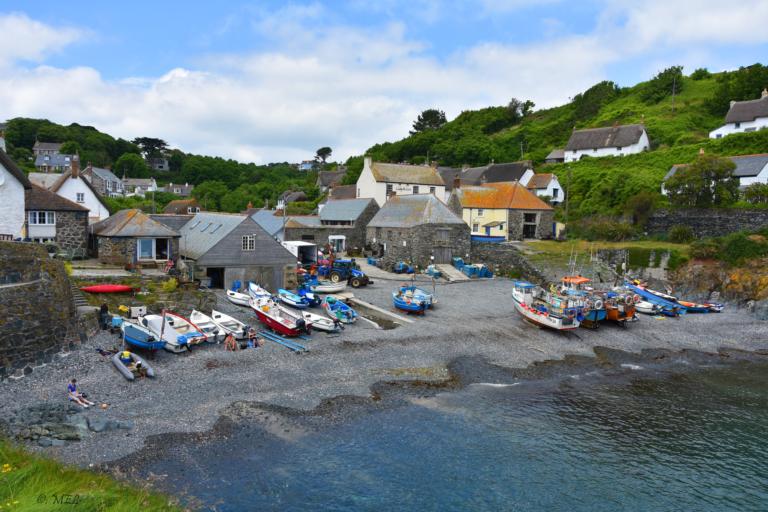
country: GB
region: England
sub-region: Cornwall
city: Landewednack
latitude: 49.9871
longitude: -5.1800
